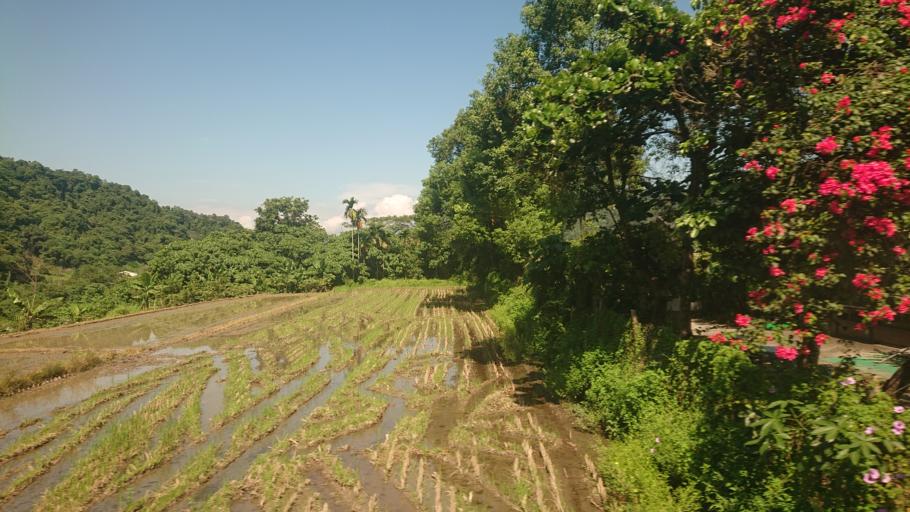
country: TW
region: Taiwan
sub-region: Nantou
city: Puli
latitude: 24.0647
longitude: 120.9531
